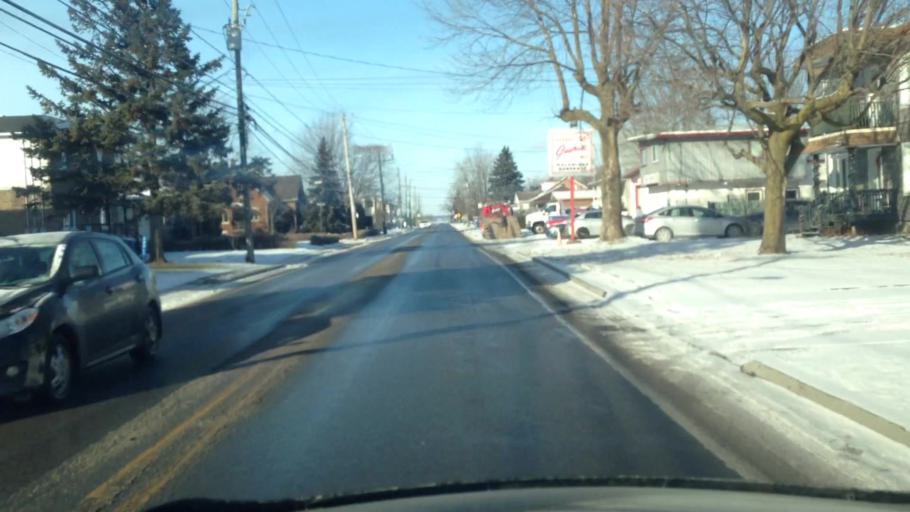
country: CA
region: Quebec
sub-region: Monteregie
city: Beauharnois
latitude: 45.3099
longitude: -73.8634
